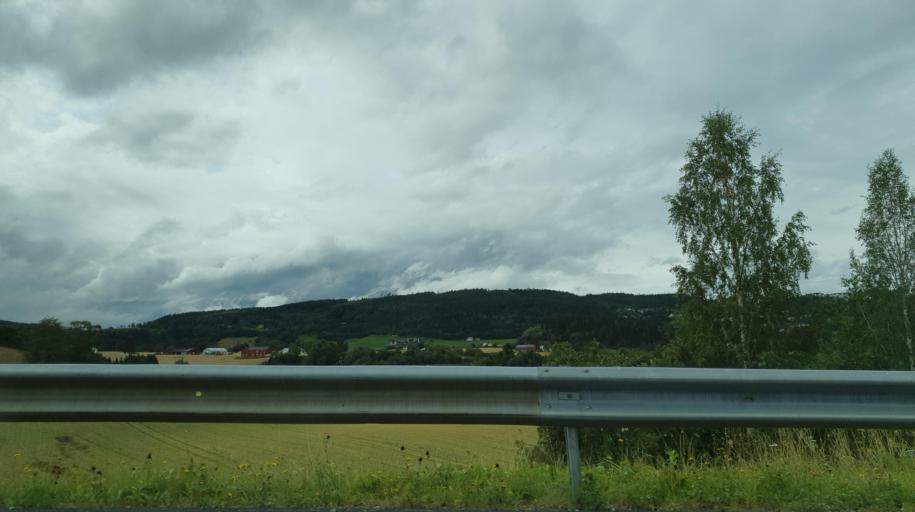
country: NO
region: Nord-Trondelag
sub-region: Stjordal
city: Stjordalshalsen
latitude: 63.4353
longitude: 10.9433
